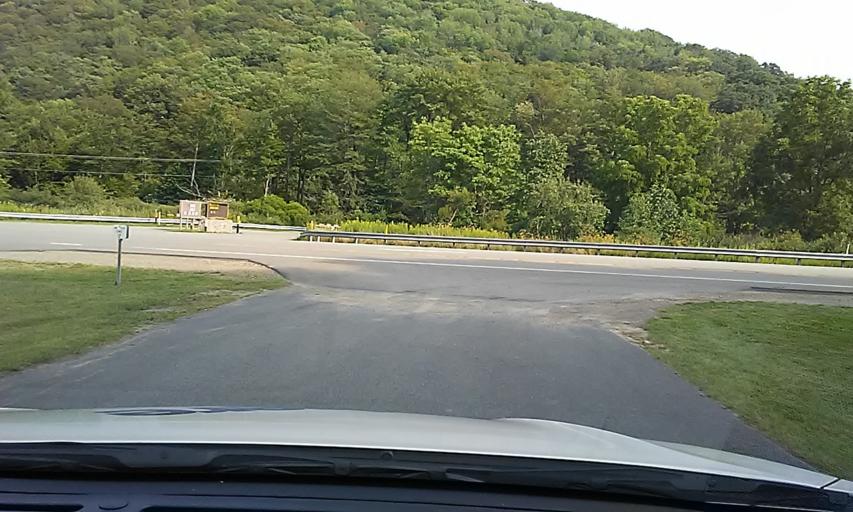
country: US
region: Pennsylvania
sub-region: Potter County
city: Coudersport
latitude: 41.7782
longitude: -77.8286
